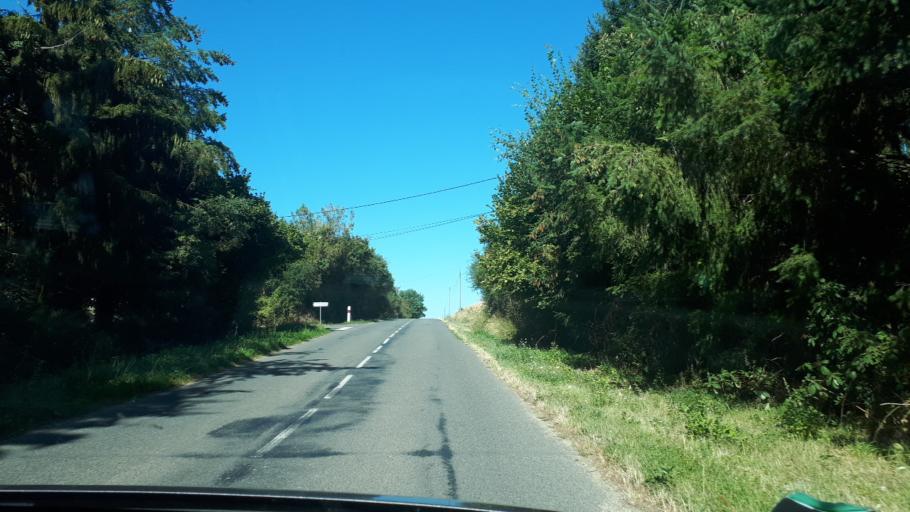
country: FR
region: Centre
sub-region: Departement du Loiret
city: Autry-le-Chatel
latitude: 47.6062
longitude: 2.5790
